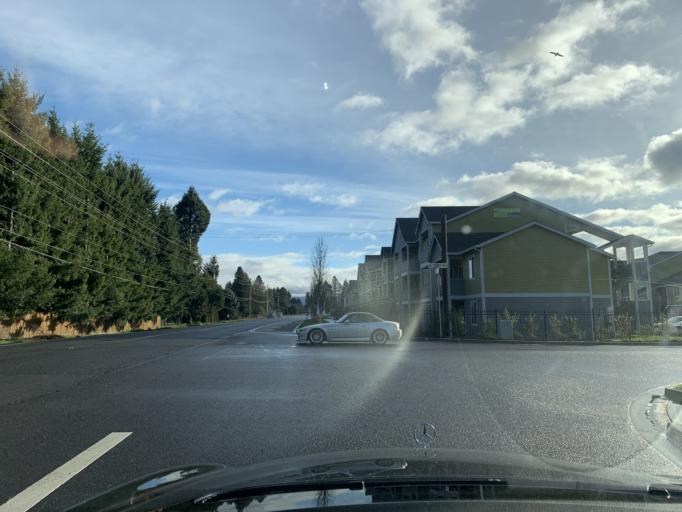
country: US
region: Washington
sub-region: Clark County
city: Brush Prairie
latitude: 45.7080
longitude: -122.5478
